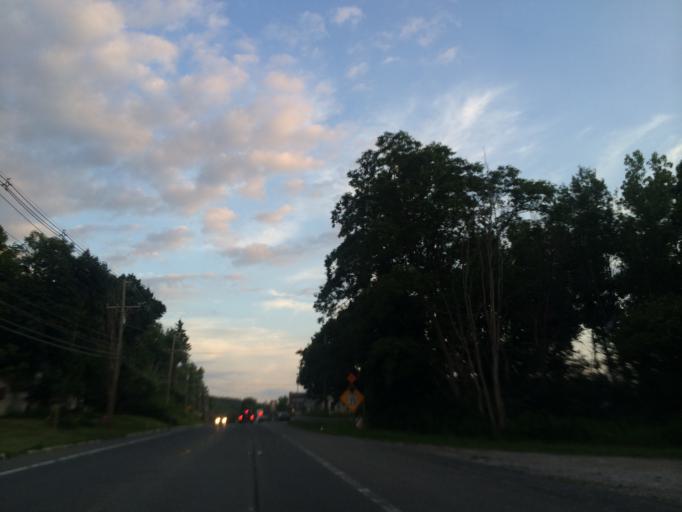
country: US
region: Massachusetts
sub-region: Berkshire County
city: Lanesborough
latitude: 42.5237
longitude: -73.2285
